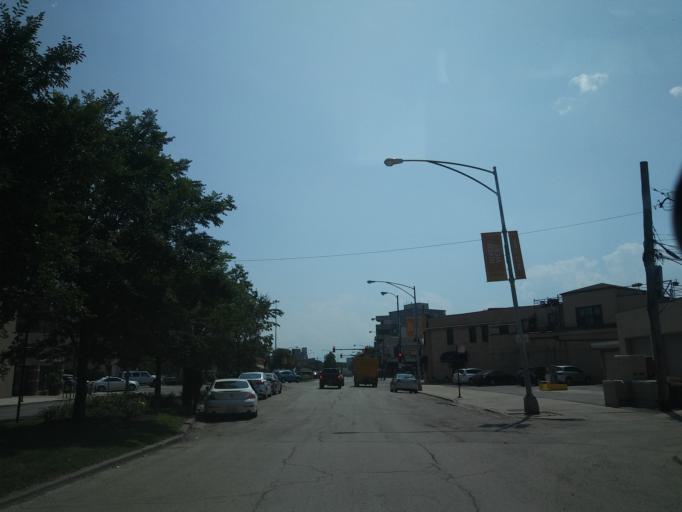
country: US
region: Illinois
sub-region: Cook County
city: Chicago
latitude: 41.8969
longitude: -87.6542
